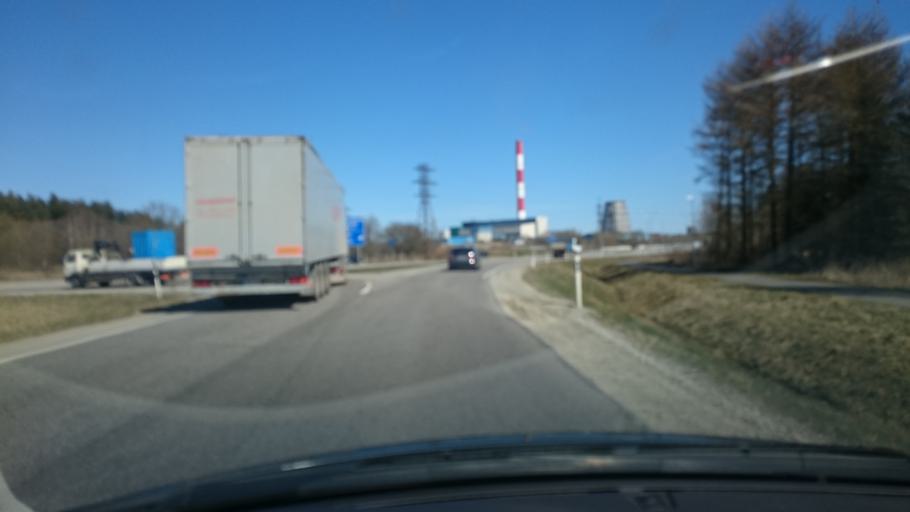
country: EE
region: Harju
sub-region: Tallinna linn
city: Kose
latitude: 59.4432
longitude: 24.9112
